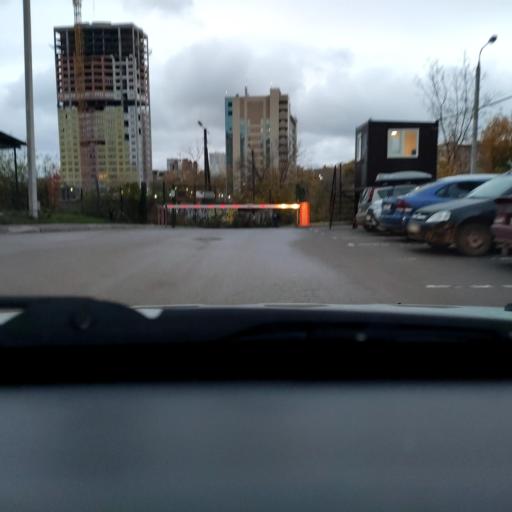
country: RU
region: Perm
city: Perm
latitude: 57.9996
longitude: 56.2025
